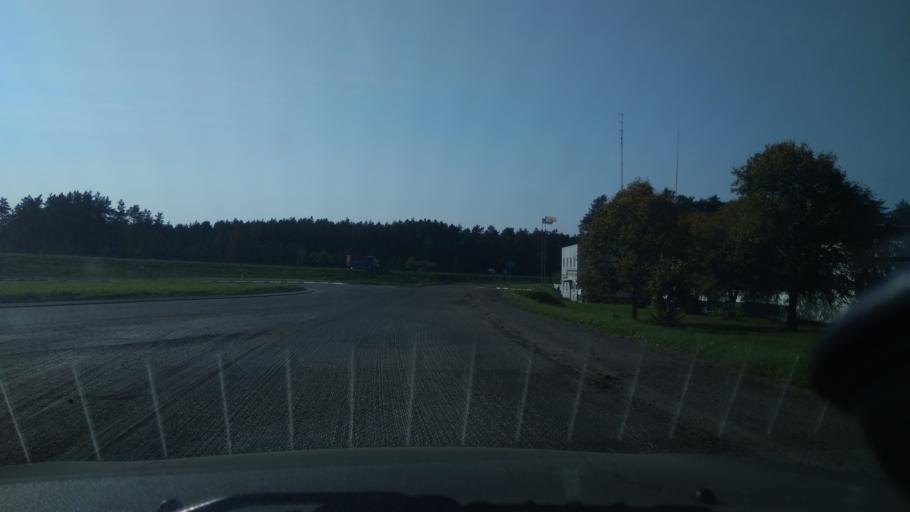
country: BY
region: Minsk
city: Rakaw
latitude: 53.9798
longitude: 27.0408
